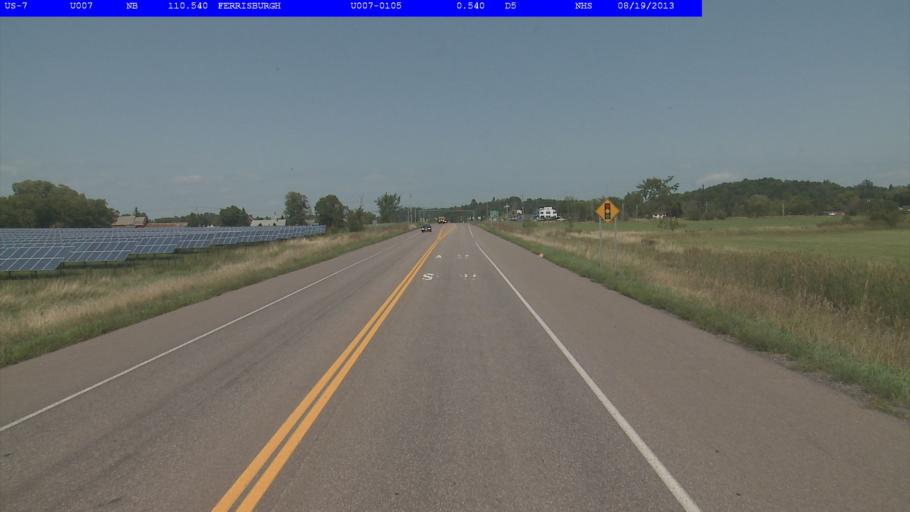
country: US
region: Vermont
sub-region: Addison County
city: Vergennes
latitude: 44.1694
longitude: -73.2393
